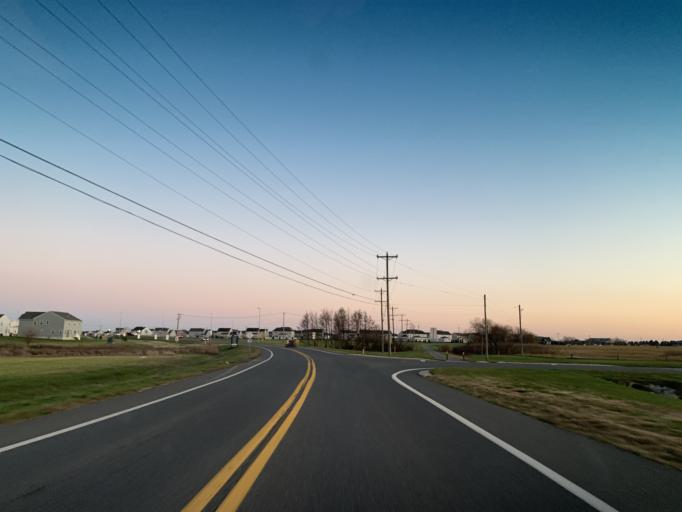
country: US
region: Delaware
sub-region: New Castle County
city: Middletown
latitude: 39.4301
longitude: -75.7419
